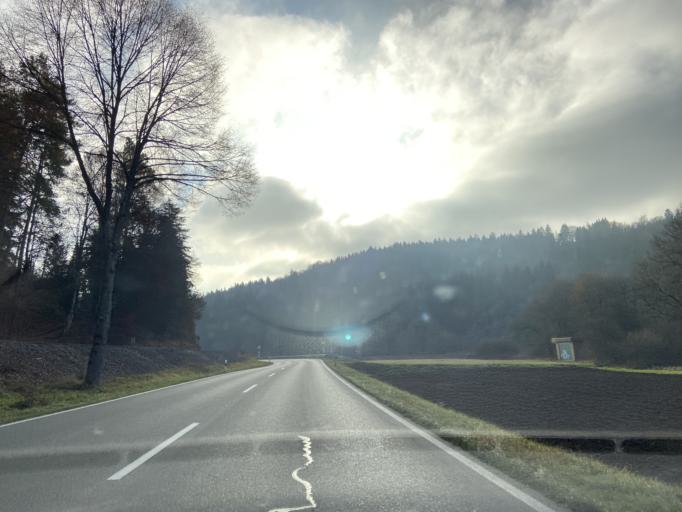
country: DE
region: Baden-Wuerttemberg
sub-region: Tuebingen Region
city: Gammertingen
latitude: 48.2378
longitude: 9.2249
